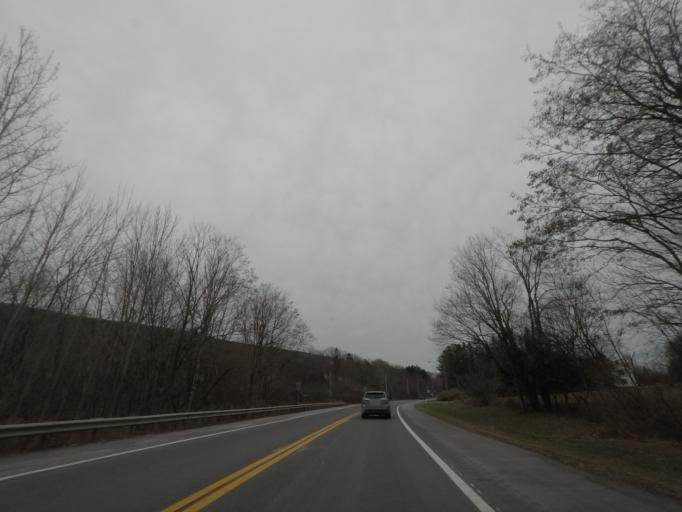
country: US
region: Massachusetts
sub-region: Berkshire County
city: Lanesborough
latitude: 42.5431
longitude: -73.3164
